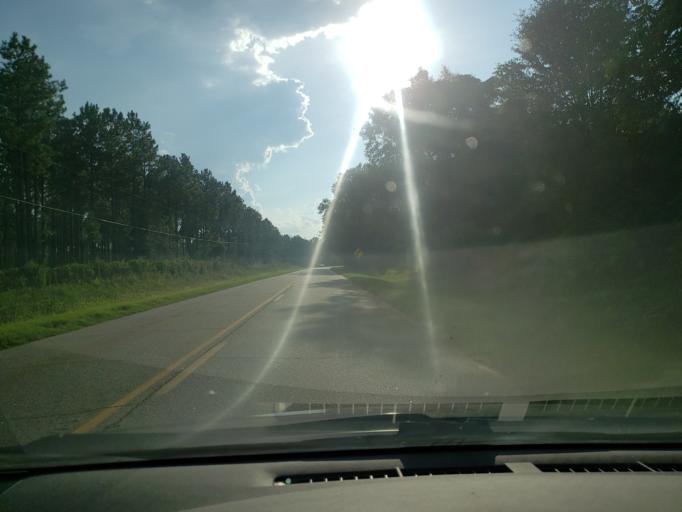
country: US
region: Georgia
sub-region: Dougherty County
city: Albany
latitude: 31.5730
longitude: -84.3272
